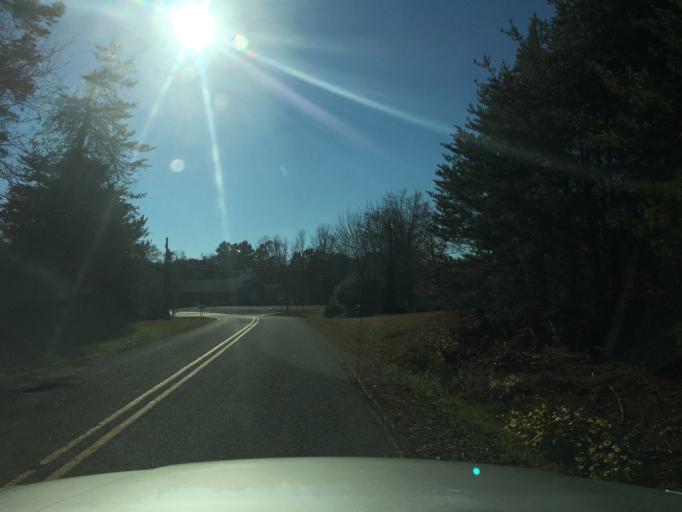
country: US
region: North Carolina
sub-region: Rutherford County
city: Rutherfordton
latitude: 35.2516
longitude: -82.0433
